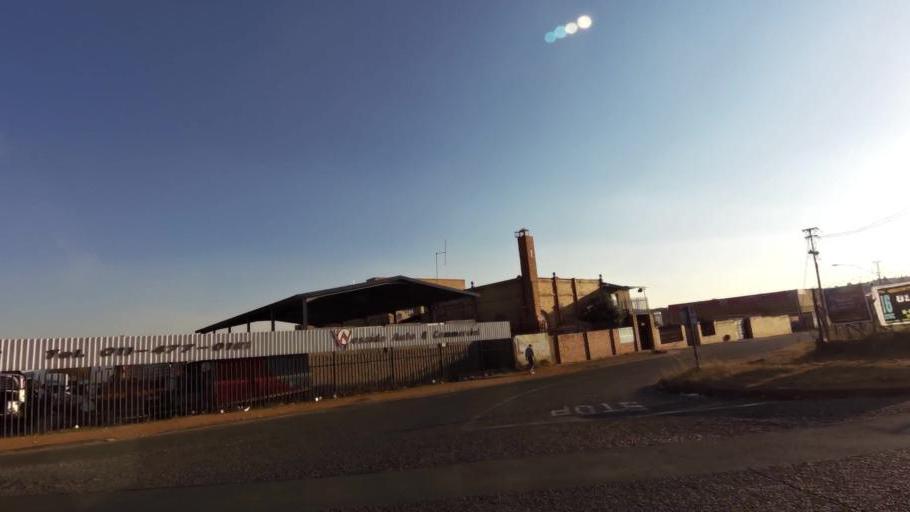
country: ZA
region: Gauteng
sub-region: City of Johannesburg Metropolitan Municipality
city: Johannesburg
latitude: -26.1756
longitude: 27.9707
